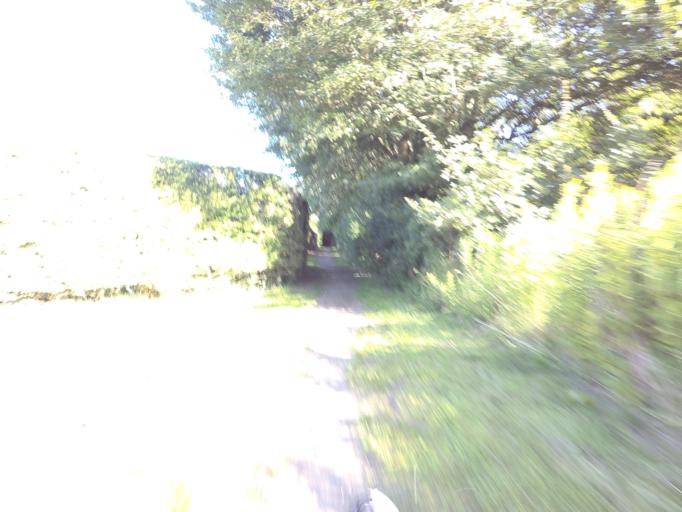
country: DK
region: Central Jutland
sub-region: Horsens Kommune
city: Horsens
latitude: 55.8750
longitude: 9.8269
